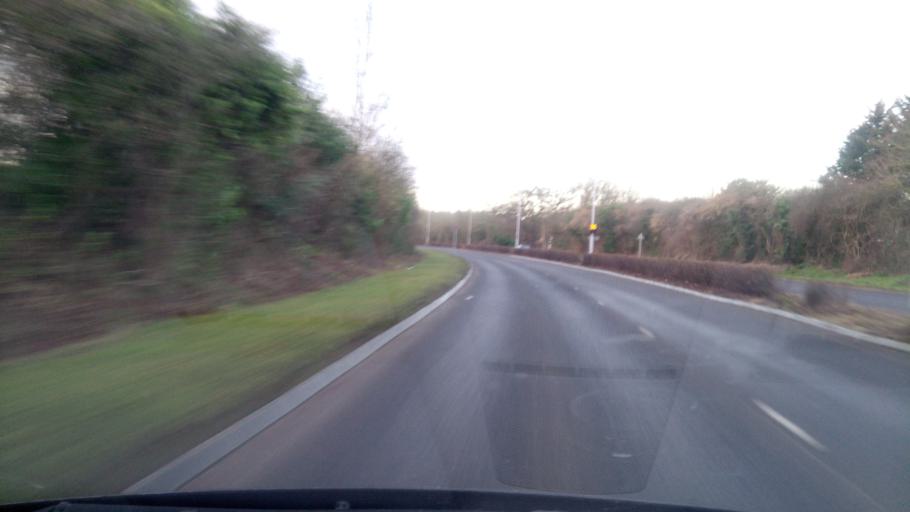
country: GB
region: England
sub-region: Peterborough
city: Marholm
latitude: 52.5756
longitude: -0.2948
